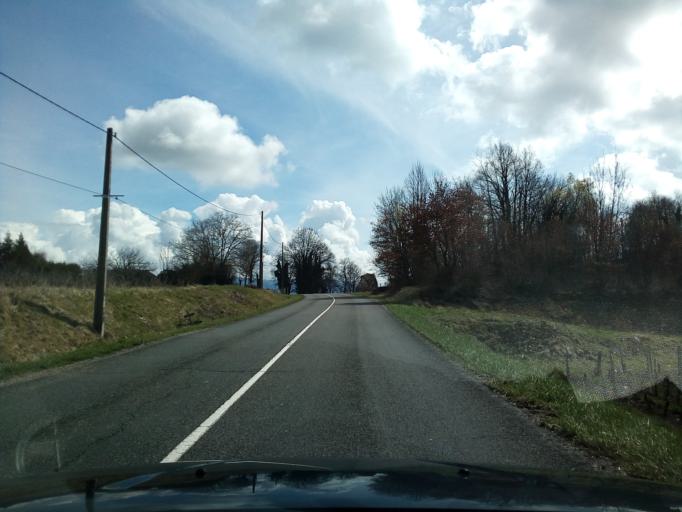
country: FR
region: Rhone-Alpes
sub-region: Departement de la Savoie
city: Les Marches
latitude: 45.4959
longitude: 5.9722
